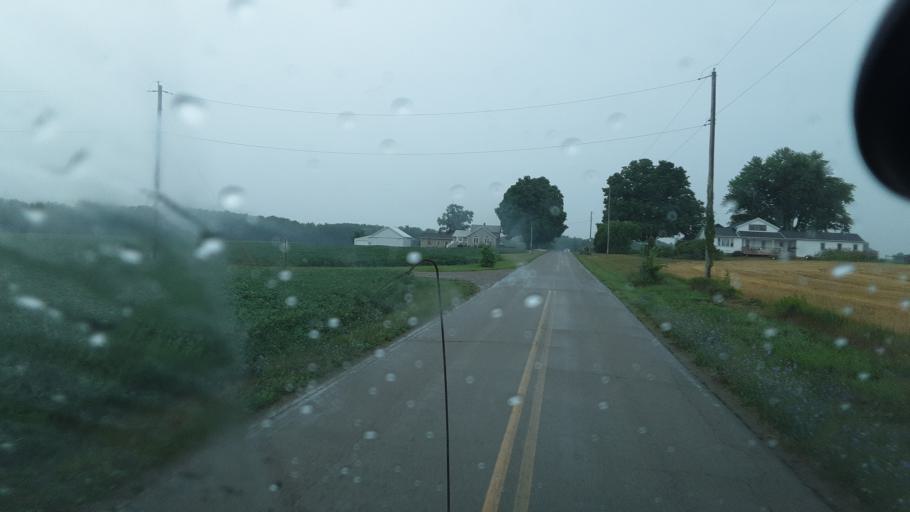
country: US
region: Ohio
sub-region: Williams County
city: Edgerton
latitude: 41.4261
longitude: -84.7952
